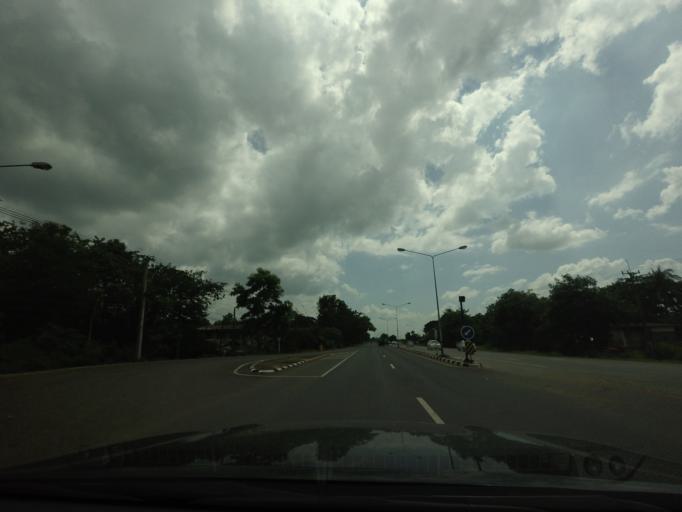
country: TH
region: Phetchabun
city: Nong Phai
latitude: 16.1916
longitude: 101.0889
